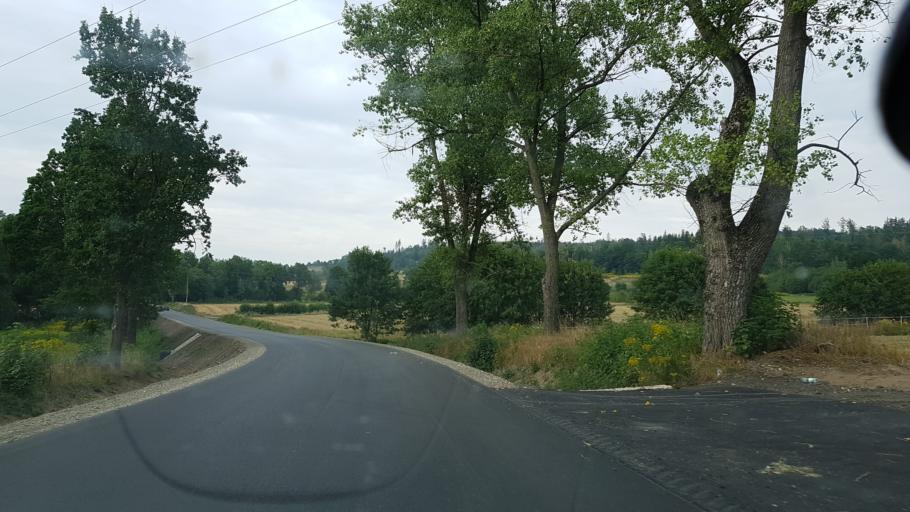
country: PL
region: Lower Silesian Voivodeship
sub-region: Powiat jeleniogorski
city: Janowice Wielkie
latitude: 50.8887
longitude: 15.9209
